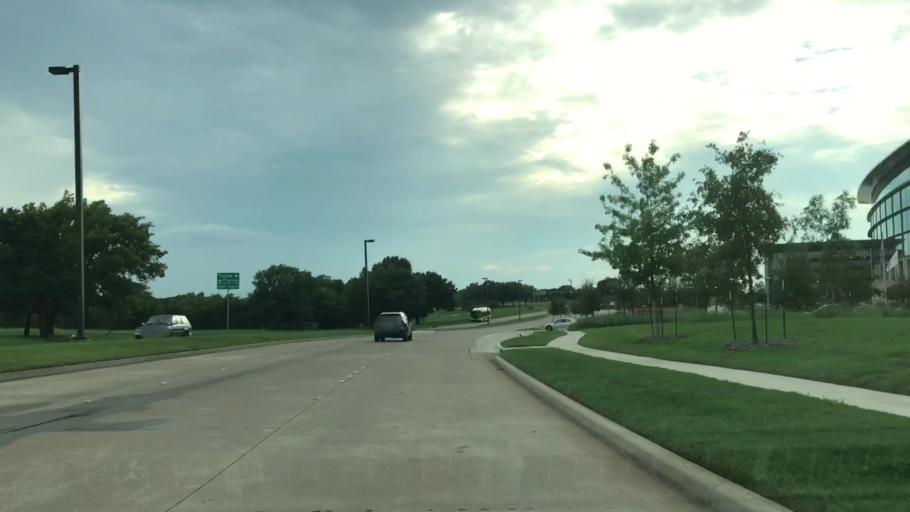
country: US
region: Texas
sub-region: Denton County
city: The Colony
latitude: 33.0808
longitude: -96.8399
